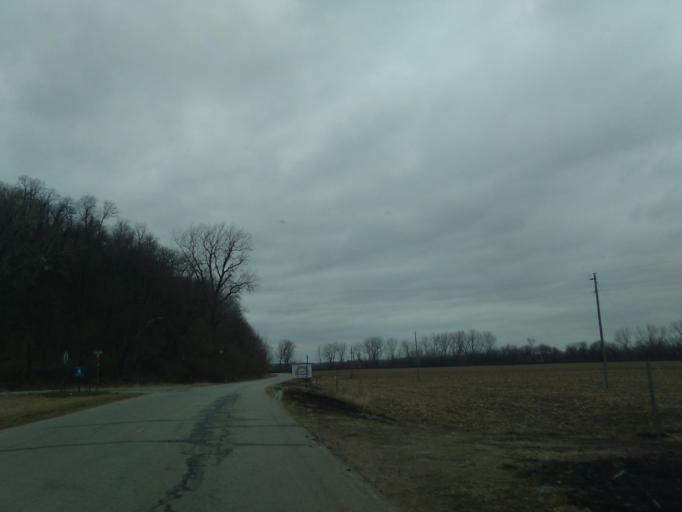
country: US
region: Missouri
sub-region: Holt County
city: Mound City
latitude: 40.0260
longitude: -95.3672
